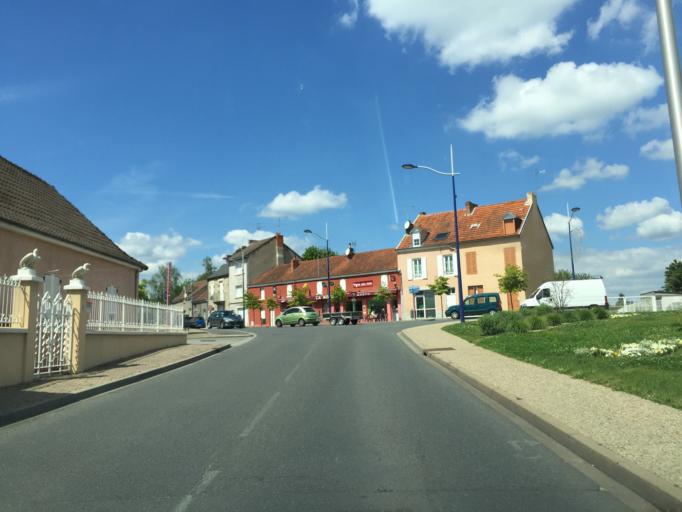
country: FR
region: Auvergne
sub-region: Departement de l'Allier
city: Bellerive-sur-Allier
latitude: 46.1172
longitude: 3.4032
